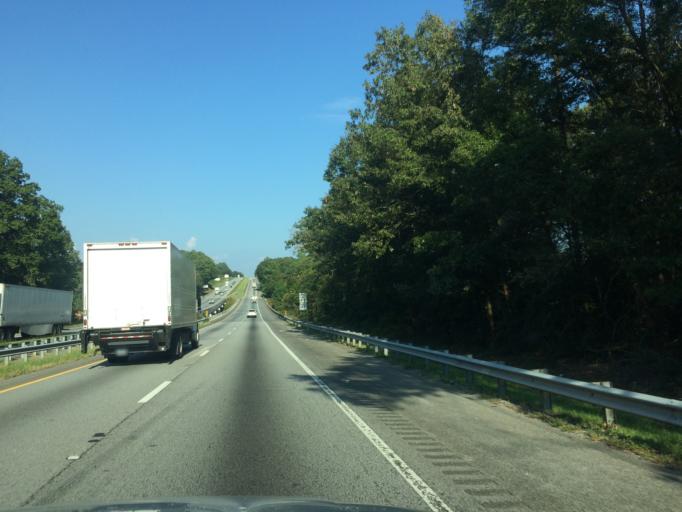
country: US
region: South Carolina
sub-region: Anderson County
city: Centerville
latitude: 34.5509
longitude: -82.7959
